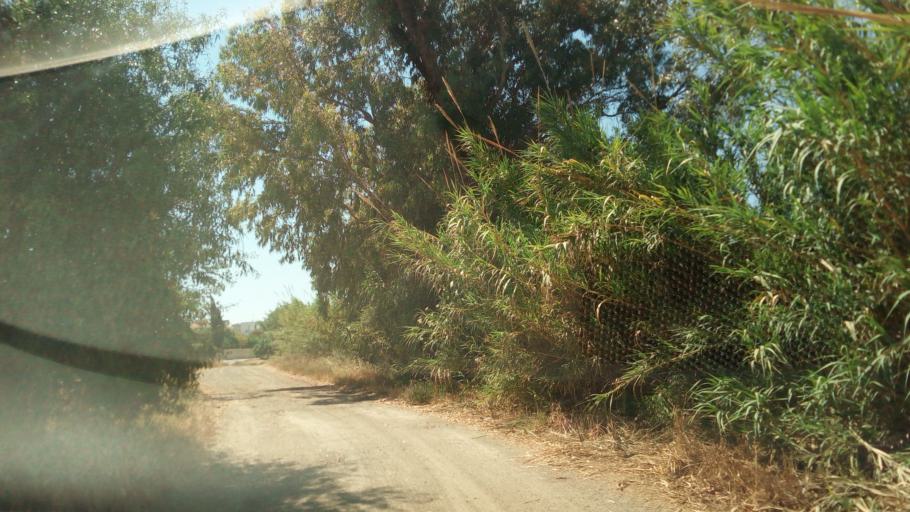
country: CY
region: Limassol
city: Pyrgos
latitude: 34.7349
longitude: 33.1813
